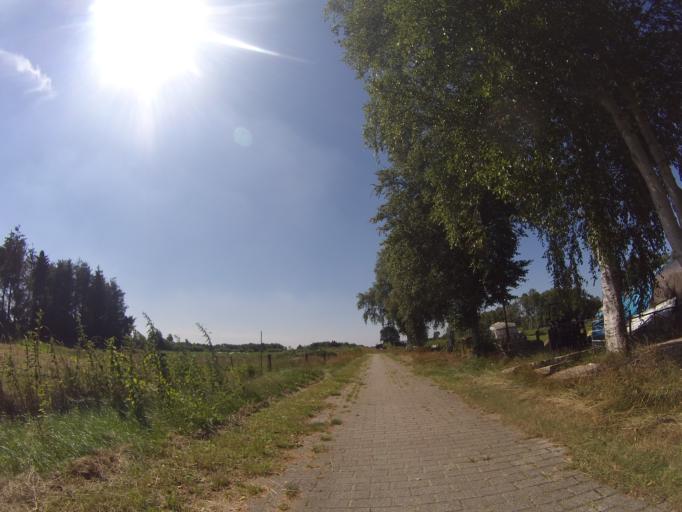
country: DE
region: Lower Saxony
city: Twist
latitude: 52.6697
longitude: 7.0167
